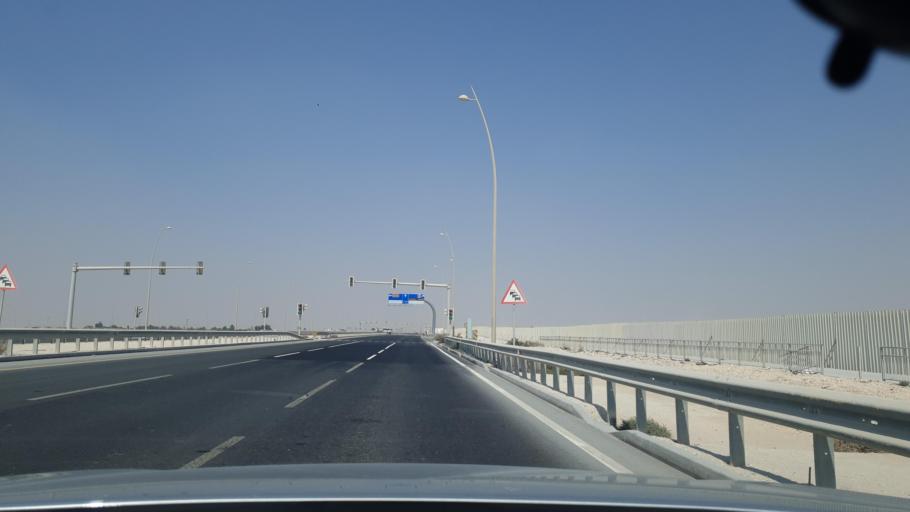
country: QA
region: Al Khawr
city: Al Khawr
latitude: 25.6623
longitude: 51.4790
